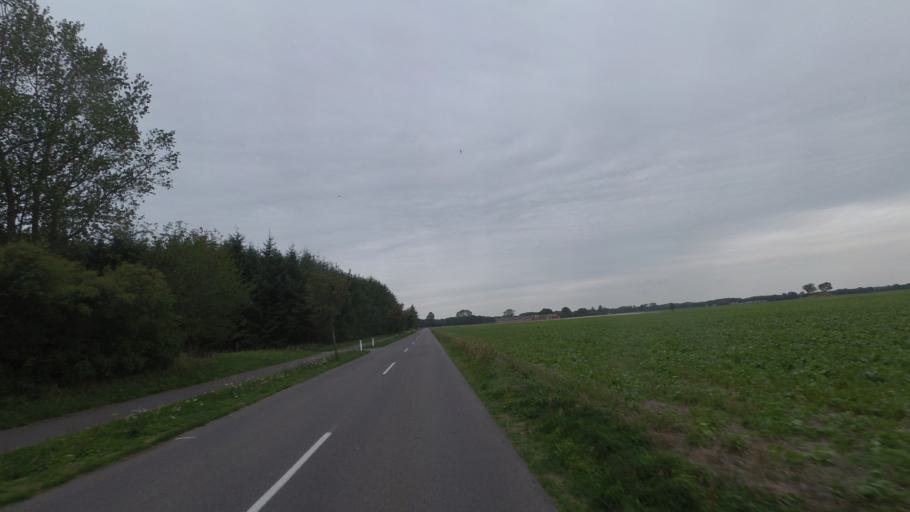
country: DK
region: Capital Region
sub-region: Bornholm Kommune
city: Akirkeby
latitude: 55.0025
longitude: 15.0149
